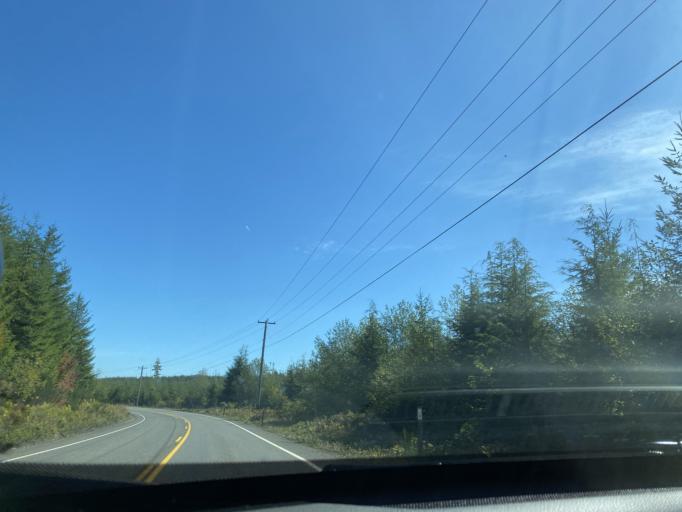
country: US
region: Washington
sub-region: Clallam County
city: Forks
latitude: 47.9629
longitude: -124.4290
